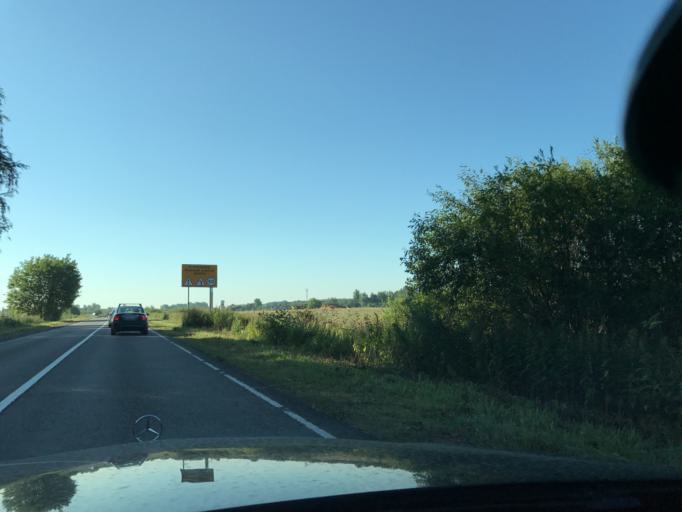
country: RU
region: Moskovskaya
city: Bakhchivandzhi
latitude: 55.8510
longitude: 38.0807
